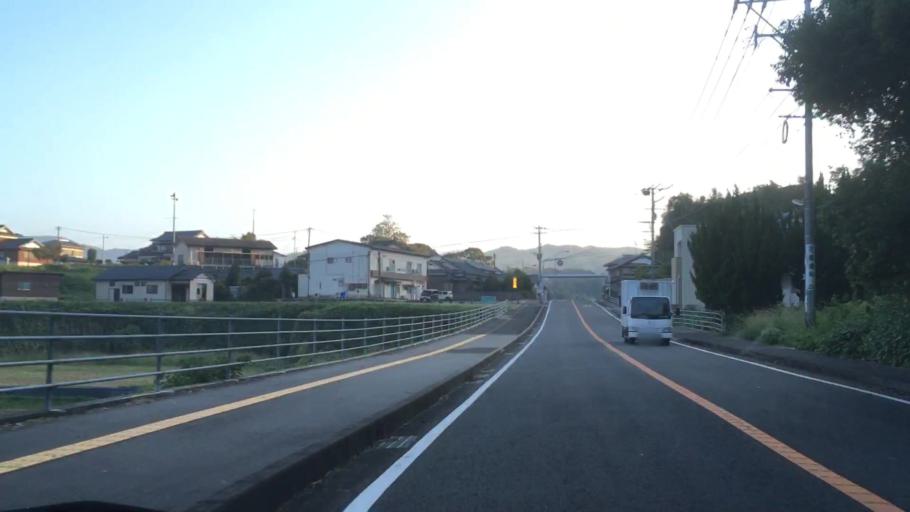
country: JP
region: Nagasaki
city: Sasebo
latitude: 33.0058
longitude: 129.7312
